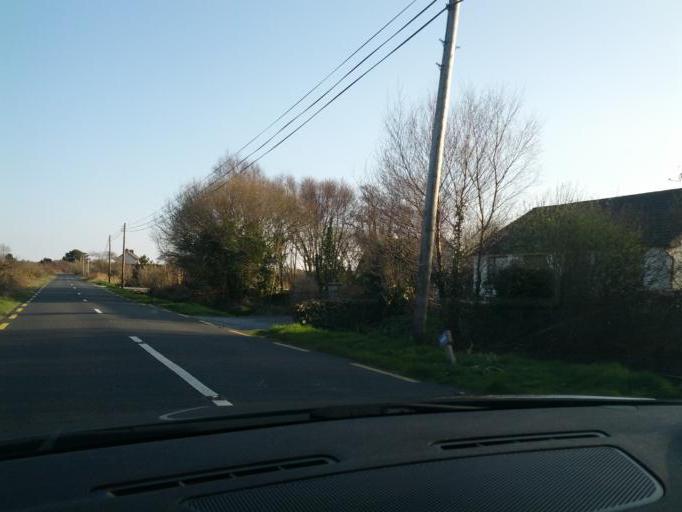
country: IE
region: Connaught
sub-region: County Galway
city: Oughterard
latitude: 53.3739
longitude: -9.5477
